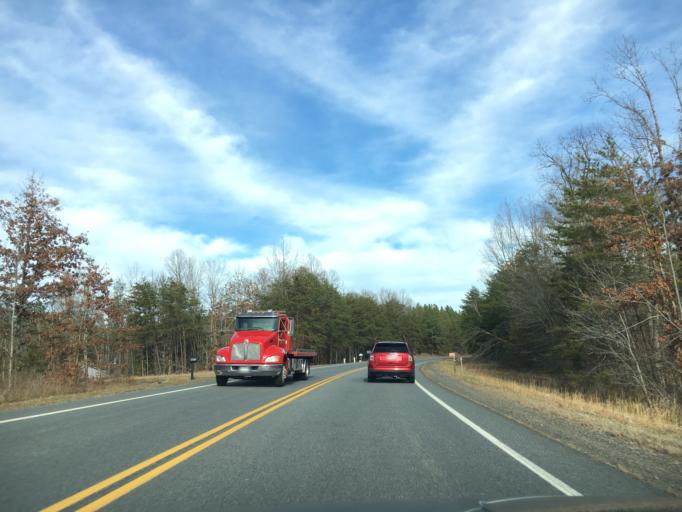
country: US
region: Virginia
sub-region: Louisa County
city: Louisa
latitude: 38.0582
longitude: -77.8812
